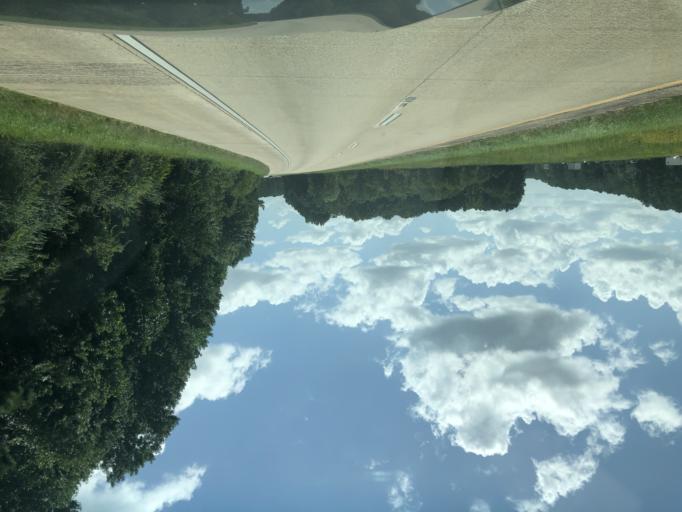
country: US
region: Georgia
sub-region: Troup County
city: Hogansville
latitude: 33.0724
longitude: -84.9299
